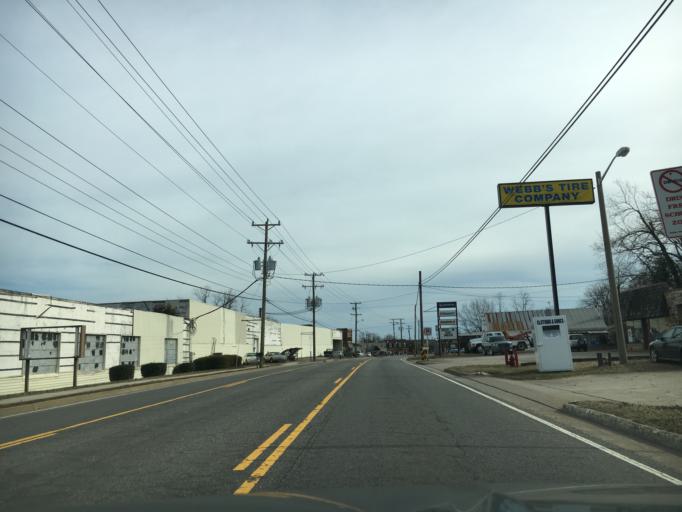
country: US
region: Virginia
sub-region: Appomattox County
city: Appomattox
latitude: 37.3593
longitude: -78.8280
